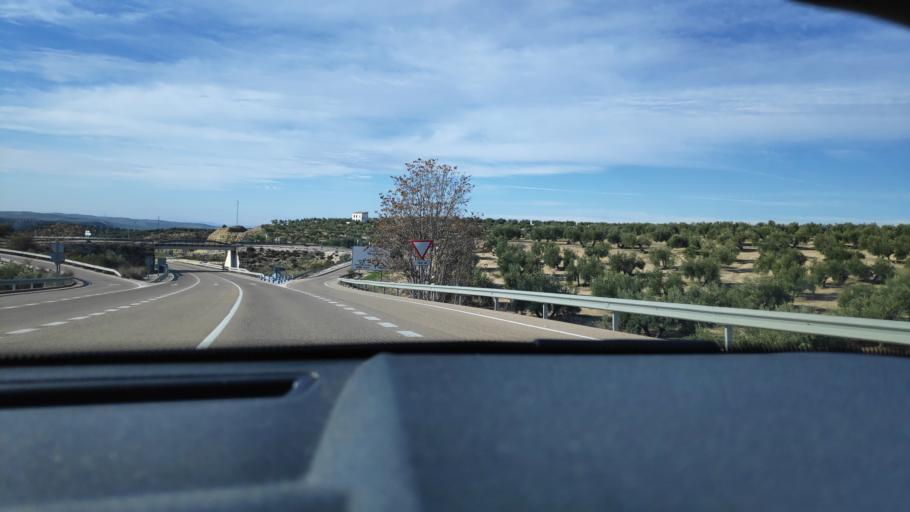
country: ES
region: Andalusia
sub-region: Provincia de Jaen
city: Porcuna
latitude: 37.8803
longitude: -4.1789
